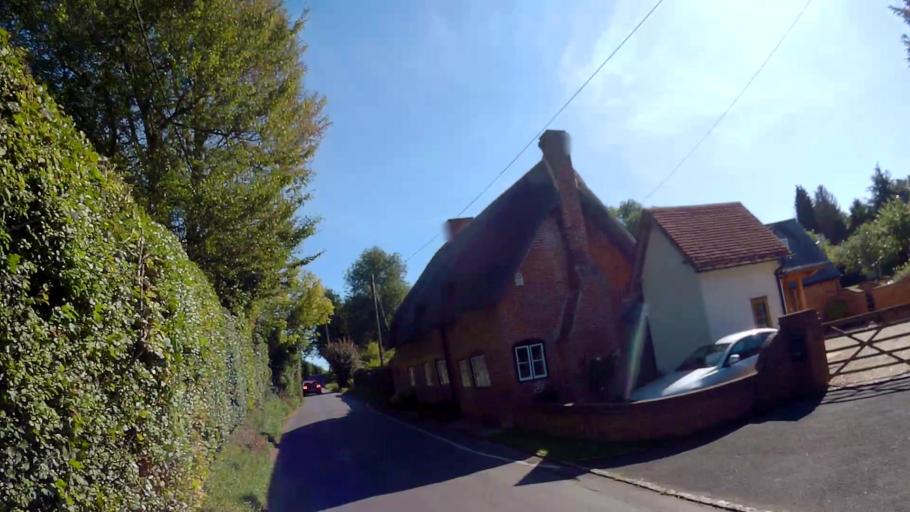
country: GB
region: England
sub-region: Hampshire
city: Andover
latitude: 51.1585
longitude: -1.4348
